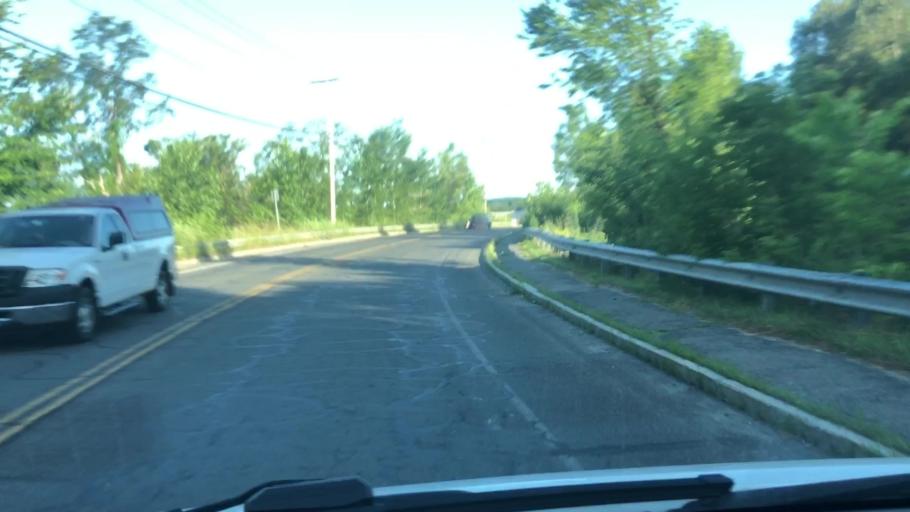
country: US
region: Massachusetts
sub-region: Berkshire County
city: Pittsfield
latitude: 42.4521
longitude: -73.2048
